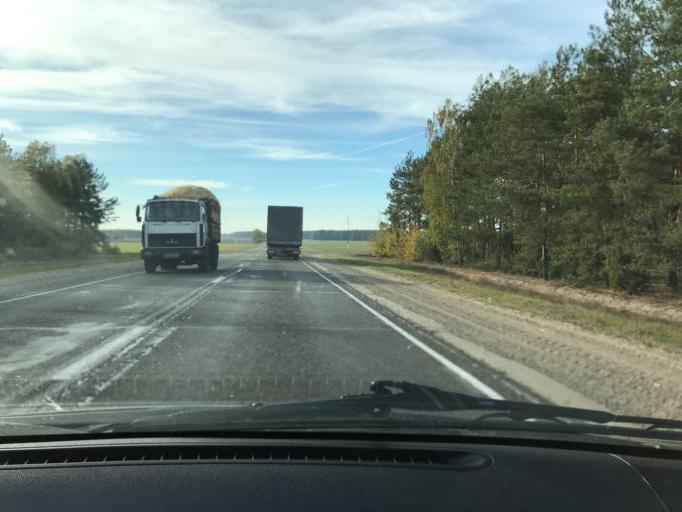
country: BY
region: Brest
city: Lahishyn
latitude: 52.1523
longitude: 25.8307
